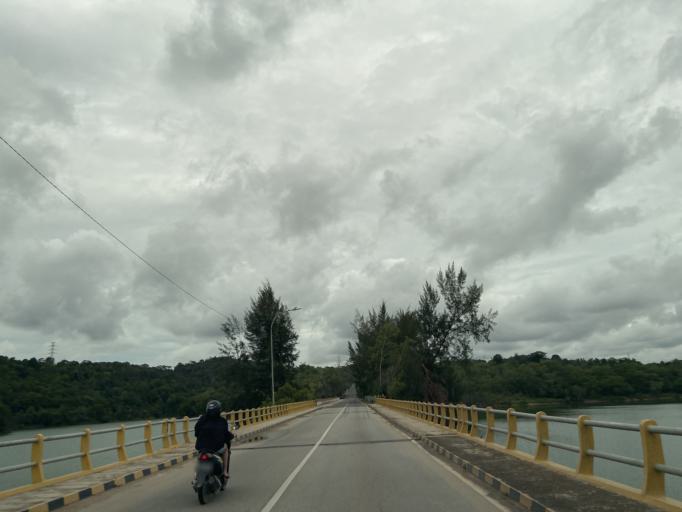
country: SG
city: Singapore
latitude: 1.1109
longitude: 104.0102
